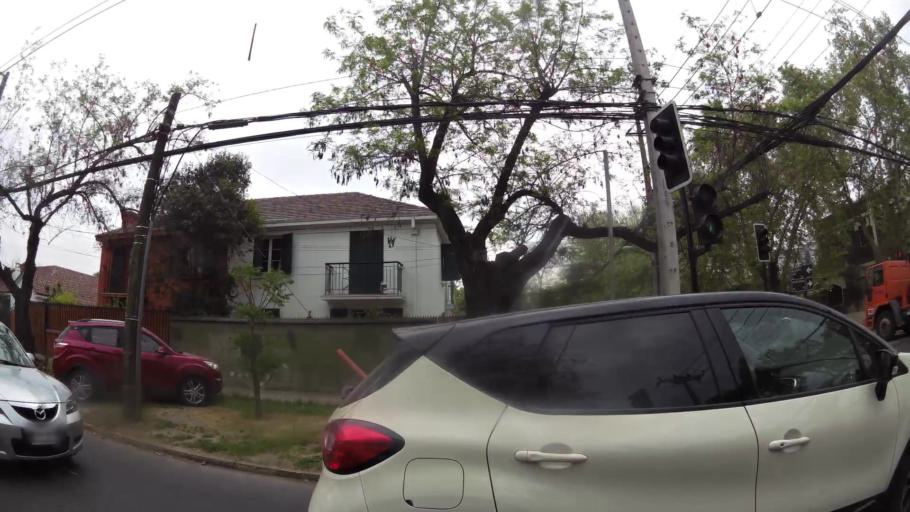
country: CL
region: Santiago Metropolitan
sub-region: Provincia de Santiago
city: Villa Presidente Frei, Nunoa, Santiago, Chile
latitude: -33.4586
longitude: -70.6032
